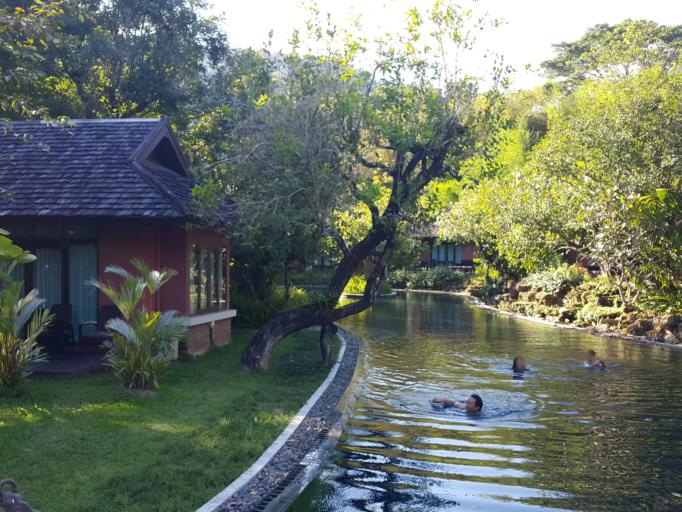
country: TH
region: Chiang Mai
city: Mae Taeng
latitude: 19.1988
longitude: 98.8838
